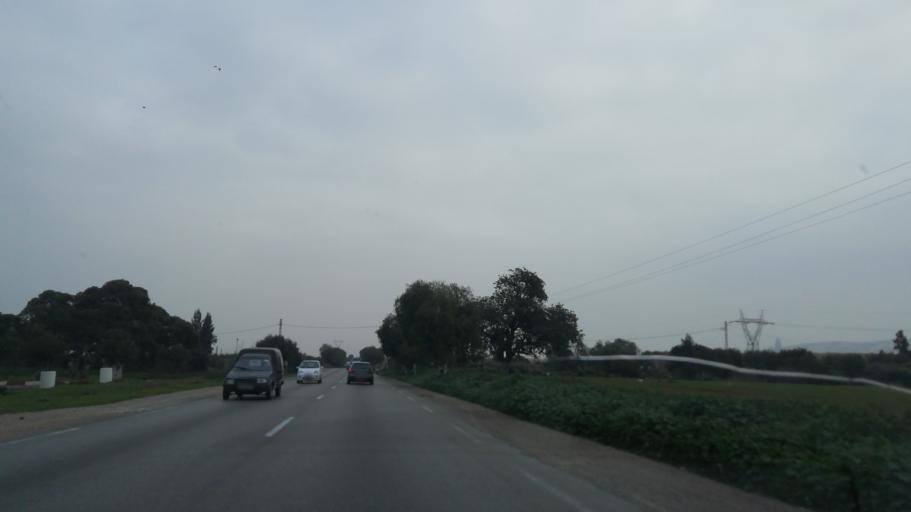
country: DZ
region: Mascara
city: Sig
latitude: 35.5439
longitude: -0.3121
